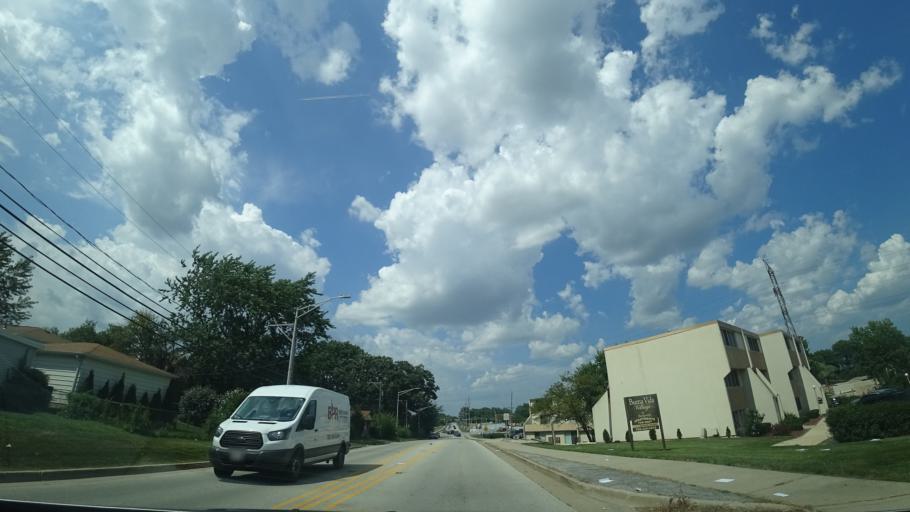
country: US
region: Illinois
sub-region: Cook County
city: Alsip
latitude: 41.6675
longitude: -87.7290
